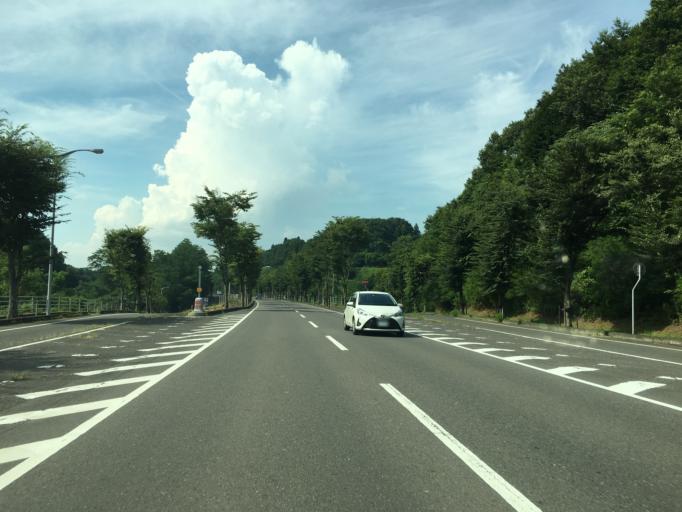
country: JP
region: Fukushima
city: Sukagawa
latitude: 37.2417
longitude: 140.4348
